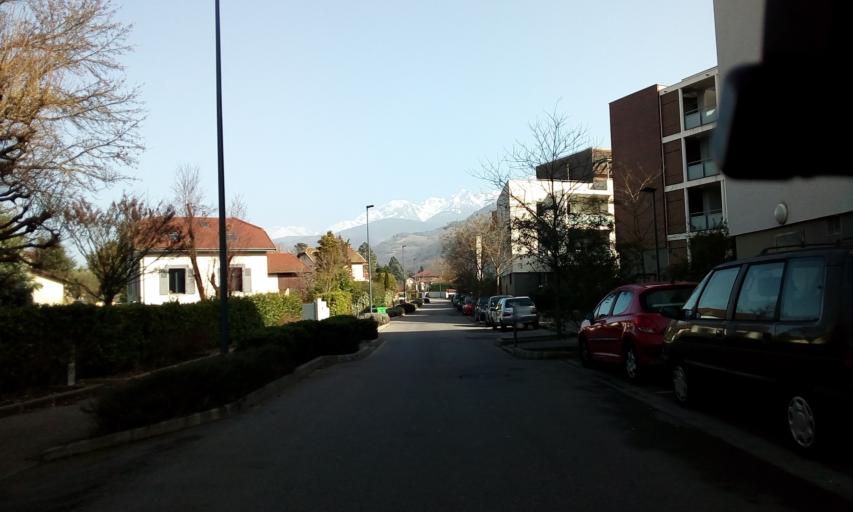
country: FR
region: Rhone-Alpes
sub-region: Departement de l'Isere
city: Gieres
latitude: 45.1838
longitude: 5.7837
